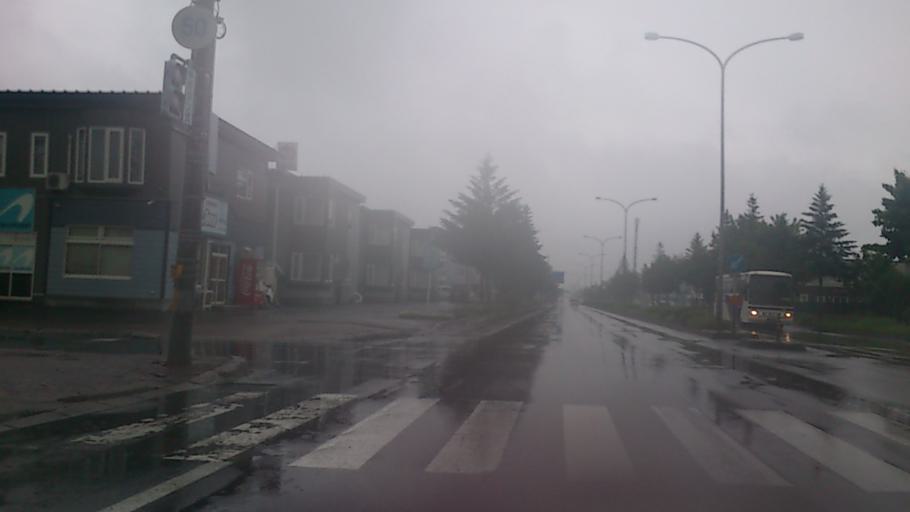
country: JP
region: Hokkaido
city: Obihiro
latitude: 42.9086
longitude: 143.1317
